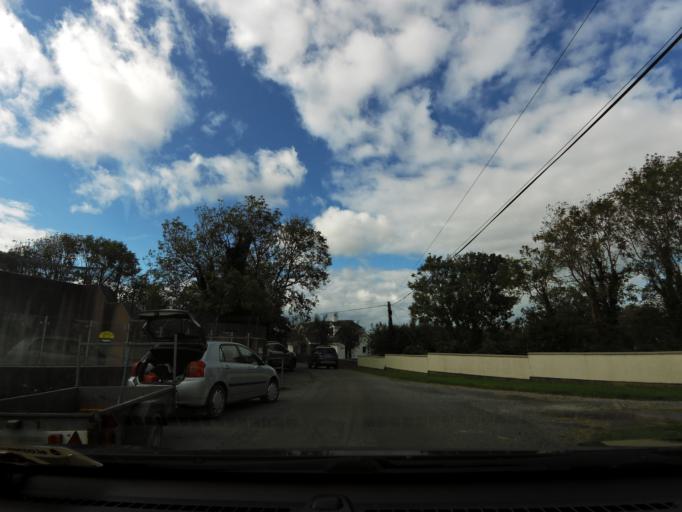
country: IE
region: Connaught
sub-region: County Galway
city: Moycullen
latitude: 53.3530
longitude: -9.1599
